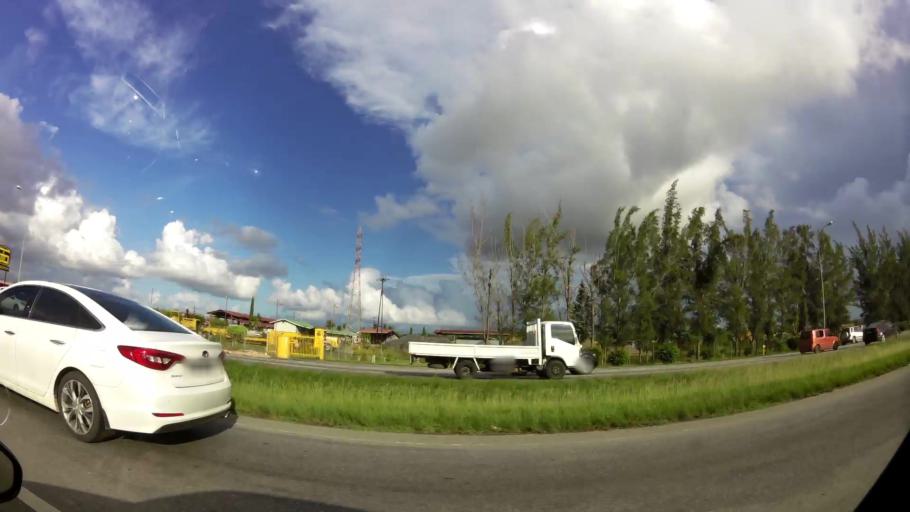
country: TT
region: Chaguanas
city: Chaguanas
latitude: 10.4929
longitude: -61.4062
